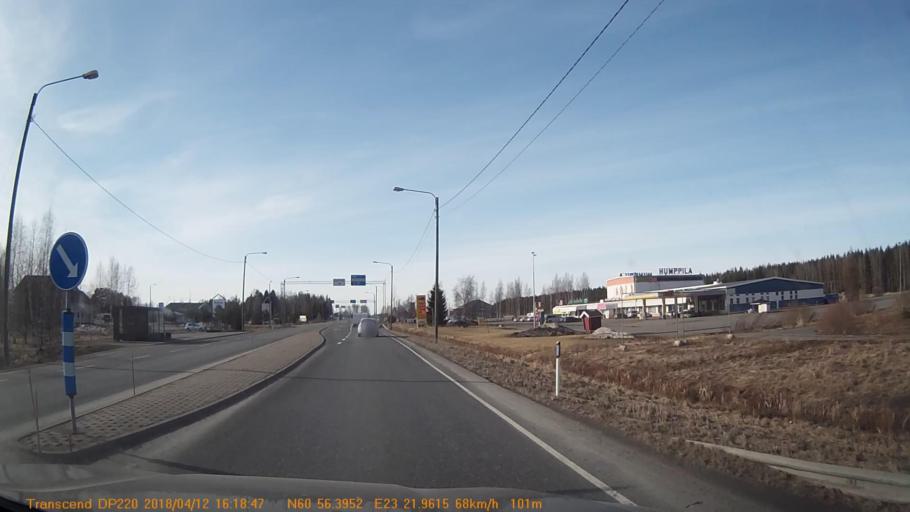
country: FI
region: Haeme
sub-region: Forssa
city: Humppila
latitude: 60.9399
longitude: 23.3661
